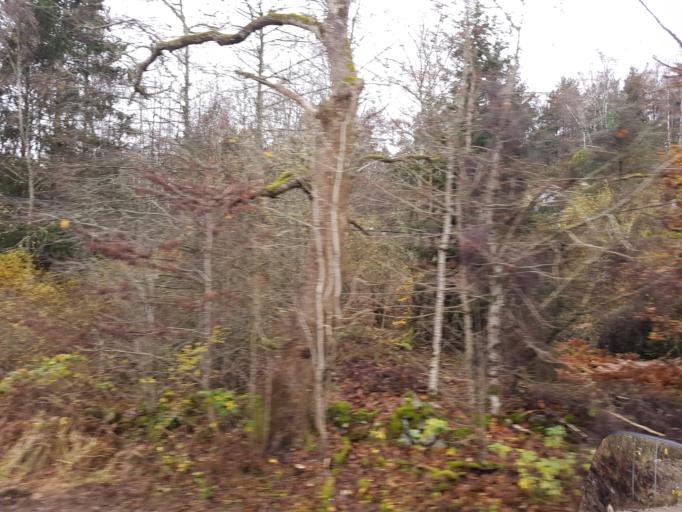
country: SE
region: Vaestra Goetaland
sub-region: Orust
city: Henan
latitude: 58.2364
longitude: 11.7333
